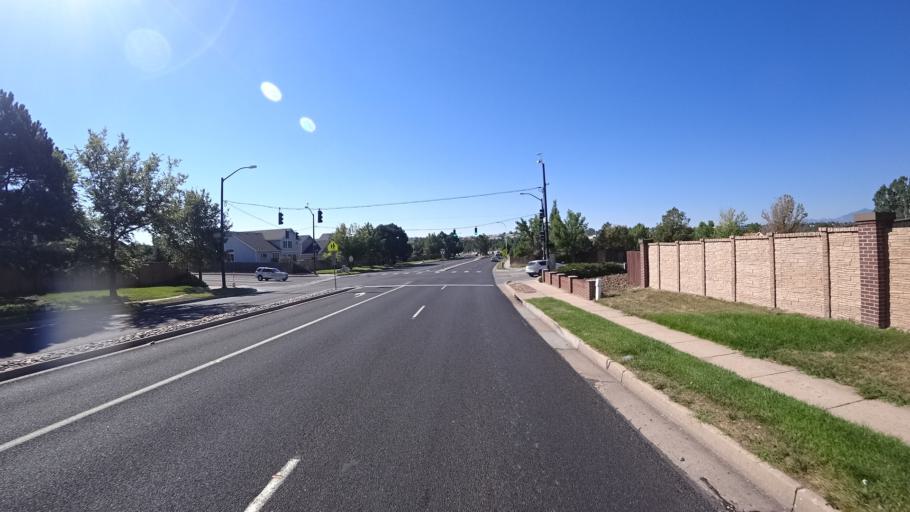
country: US
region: Colorado
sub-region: El Paso County
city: Cimarron Hills
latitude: 38.9331
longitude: -104.7542
